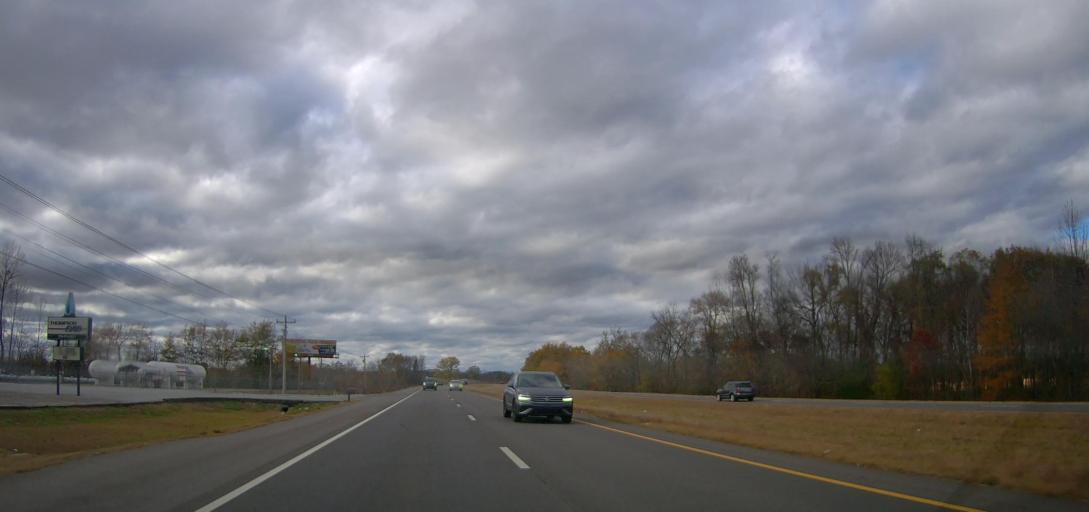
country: US
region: Alabama
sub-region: Lawrence County
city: Moulton
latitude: 34.4655
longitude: -87.2580
